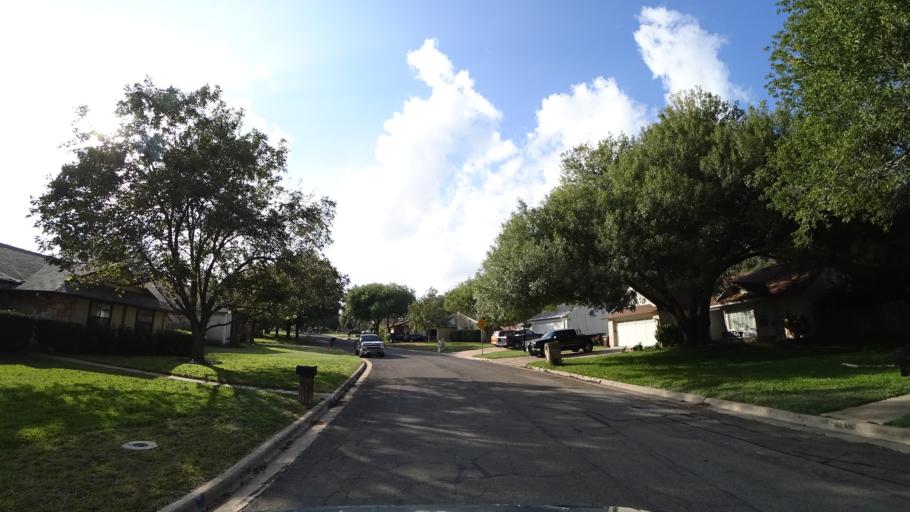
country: US
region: Texas
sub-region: Williamson County
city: Round Rock
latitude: 30.4926
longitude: -97.6681
